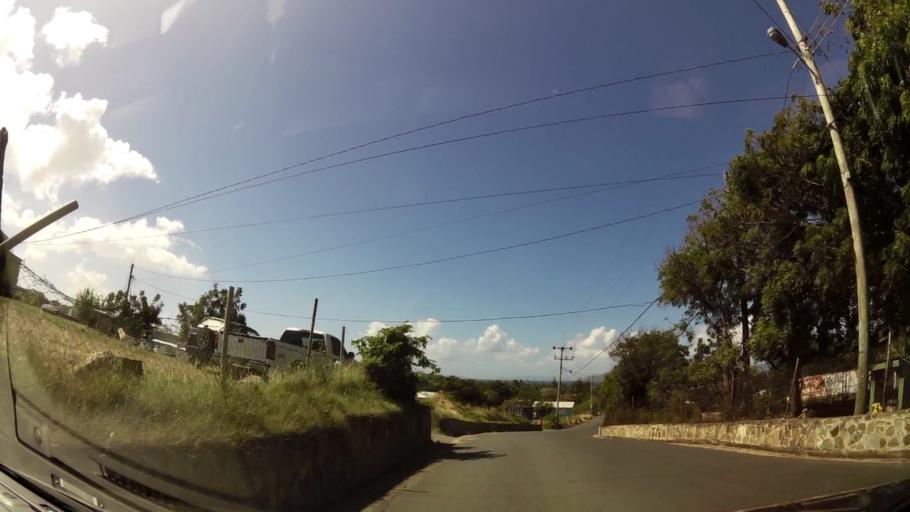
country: VG
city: Tortola
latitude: 18.4532
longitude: -64.4317
